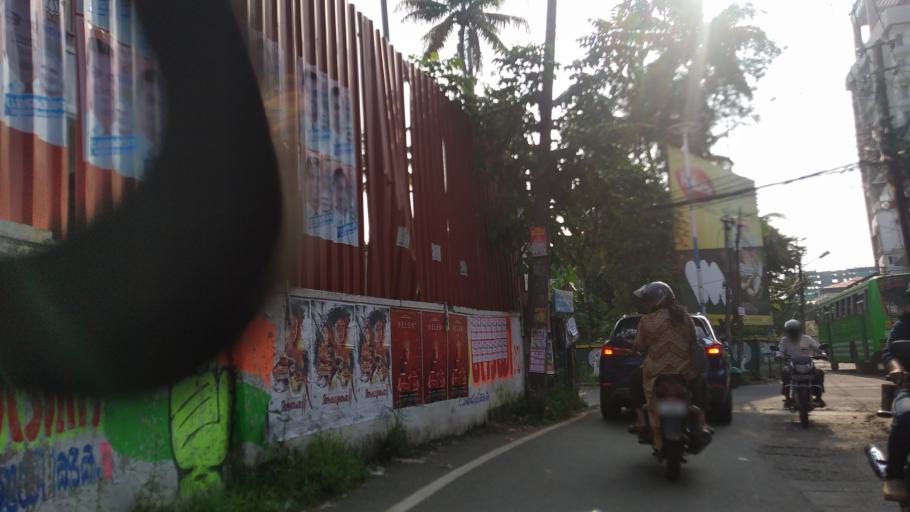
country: IN
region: Kerala
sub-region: Ernakulam
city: Cochin
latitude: 9.9973
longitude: 76.2916
